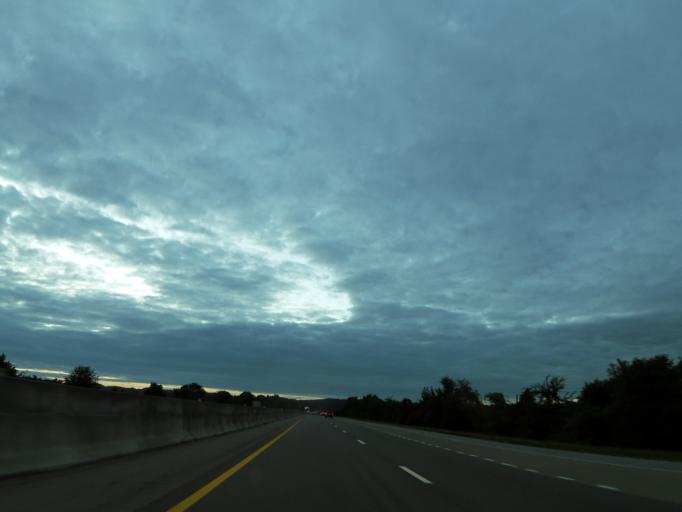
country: US
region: Tennessee
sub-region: Davidson County
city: Nashville
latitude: 36.1914
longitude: -86.8641
